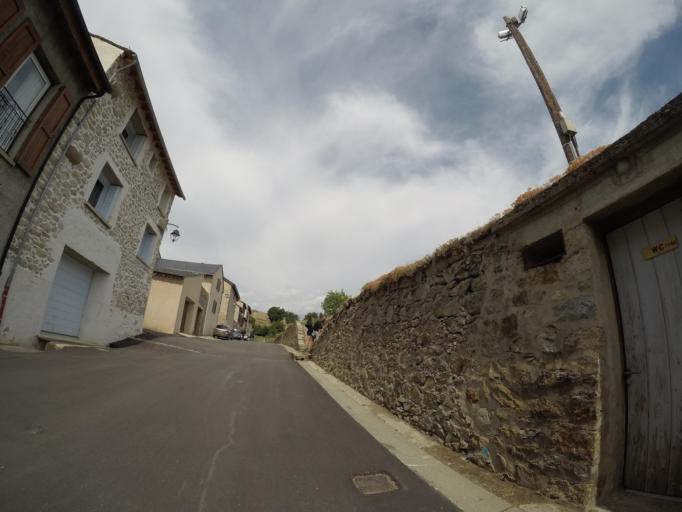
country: ES
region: Catalonia
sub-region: Provincia de Girona
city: Llivia
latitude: 42.5087
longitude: 2.1229
